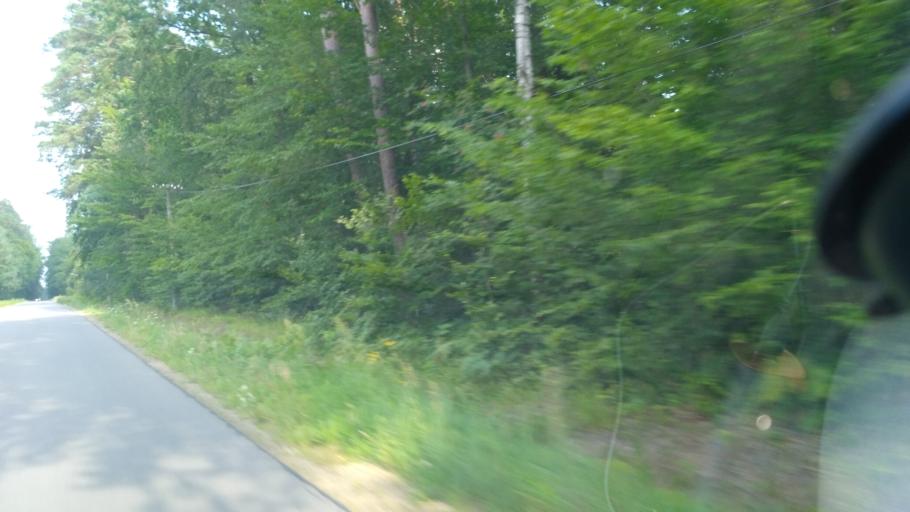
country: PL
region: Subcarpathian Voivodeship
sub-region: Powiat rzeszowski
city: Wysoka Glogowska
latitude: 50.1614
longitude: 21.9945
